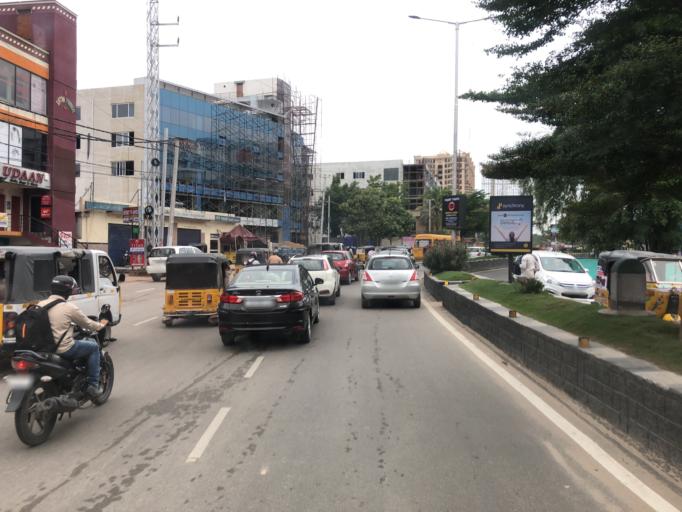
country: IN
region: Telangana
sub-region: Rangareddi
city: Kukatpalli
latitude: 17.4584
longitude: 78.3660
